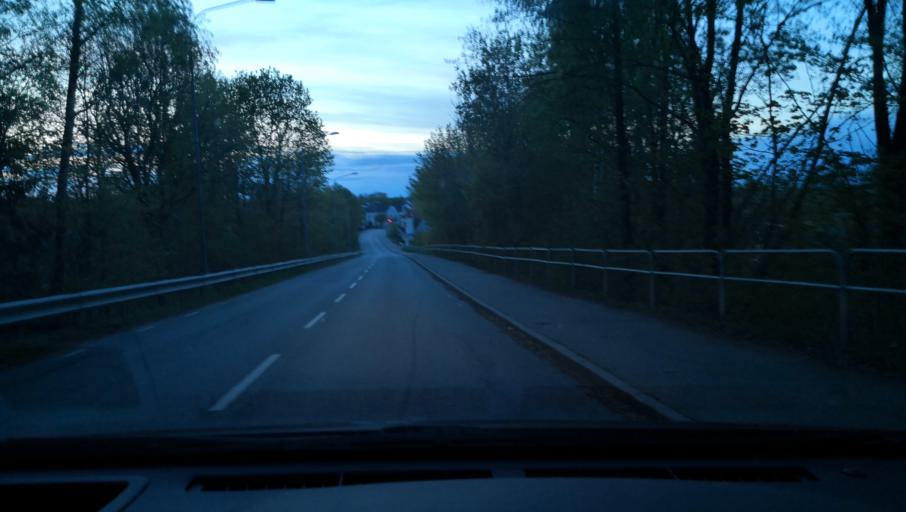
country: SE
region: OErebro
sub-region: Askersunds Kommun
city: Askersund
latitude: 59.0200
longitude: 14.8730
